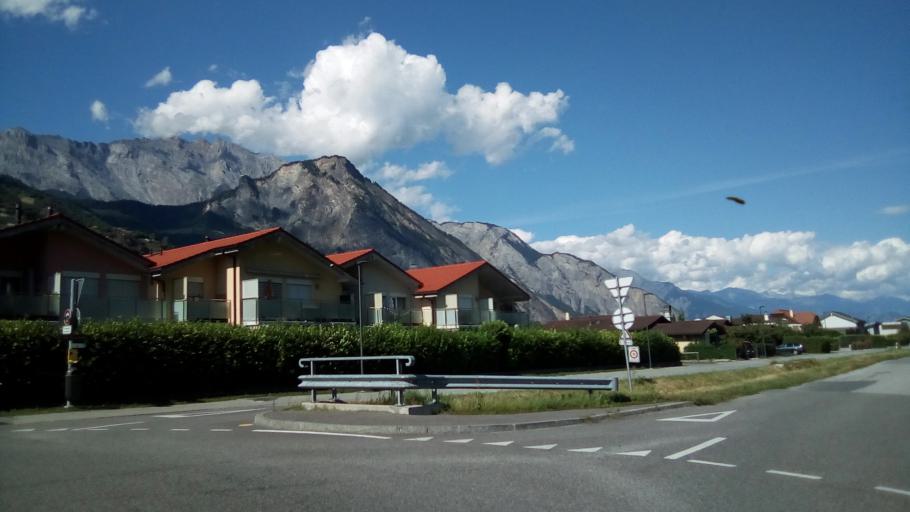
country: CH
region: Valais
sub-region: Martigny District
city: Saillon
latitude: 46.1654
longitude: 7.1844
